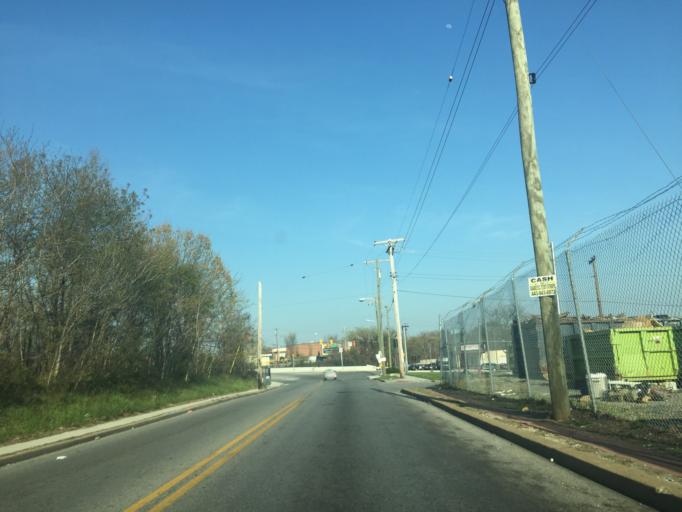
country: US
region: Maryland
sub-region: City of Baltimore
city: Baltimore
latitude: 39.3143
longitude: -76.5745
